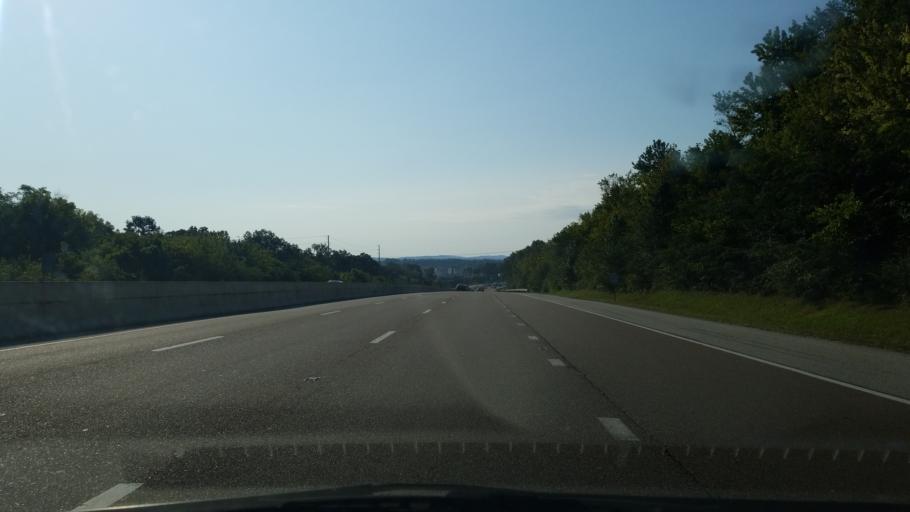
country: US
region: Tennessee
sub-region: Hamilton County
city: East Chattanooga
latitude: 35.0804
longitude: -85.2044
